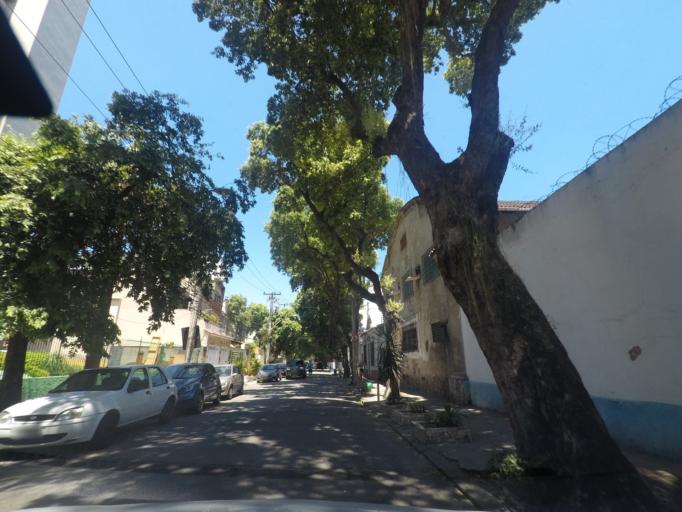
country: BR
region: Rio de Janeiro
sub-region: Rio De Janeiro
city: Rio de Janeiro
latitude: -22.9037
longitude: -43.2207
